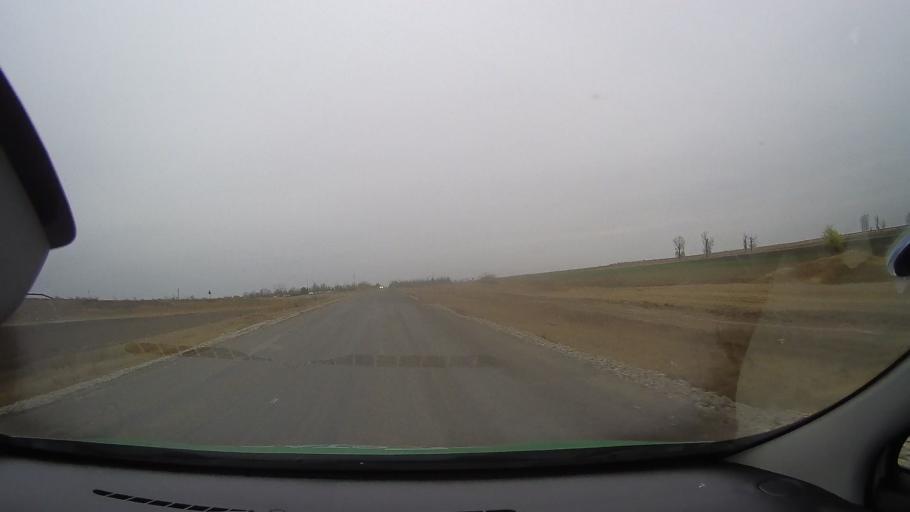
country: RO
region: Braila
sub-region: Comuna Baraganul
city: Baraganul
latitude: 44.8073
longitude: 27.5240
